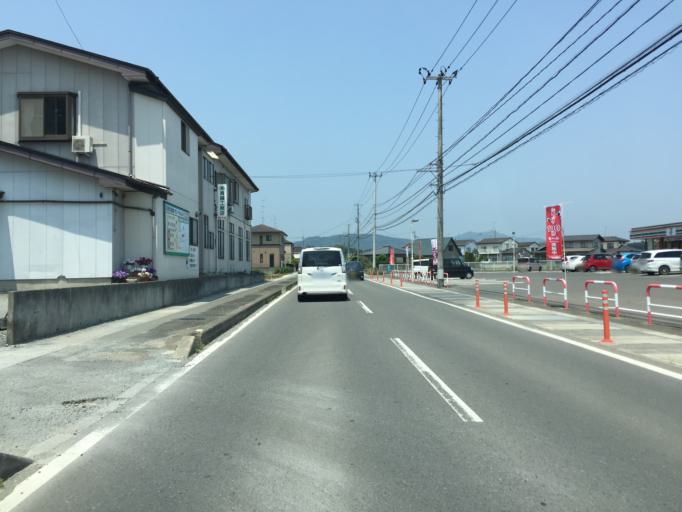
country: JP
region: Miyagi
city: Marumori
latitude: 37.8063
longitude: 140.9056
